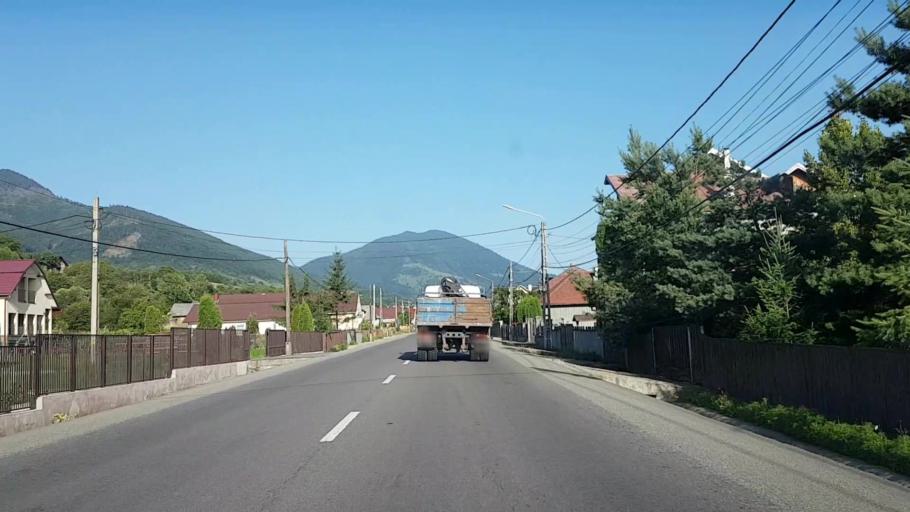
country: RO
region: Bistrita-Nasaud
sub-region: Comuna Tiha Bargaului
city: Tureac
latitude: 47.2255
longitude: 24.8142
